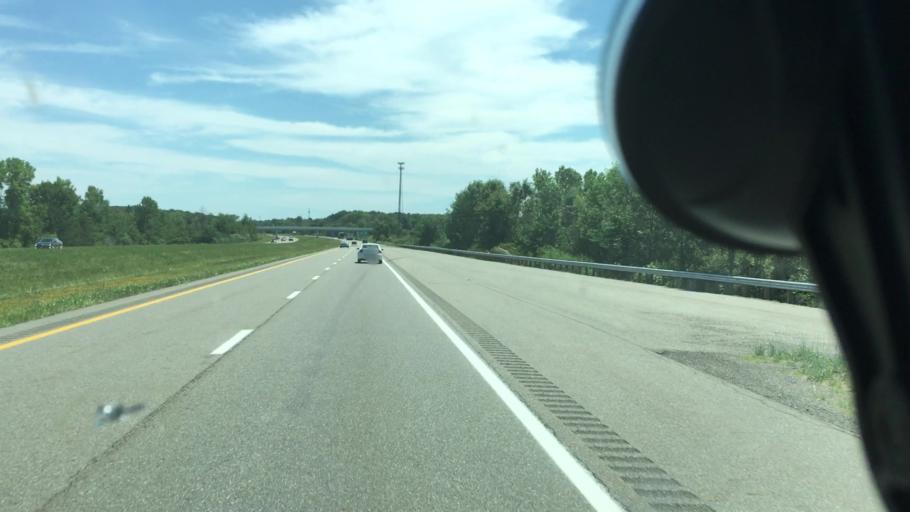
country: US
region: Ohio
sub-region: Columbiana County
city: Columbiana
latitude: 40.9493
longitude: -80.7205
